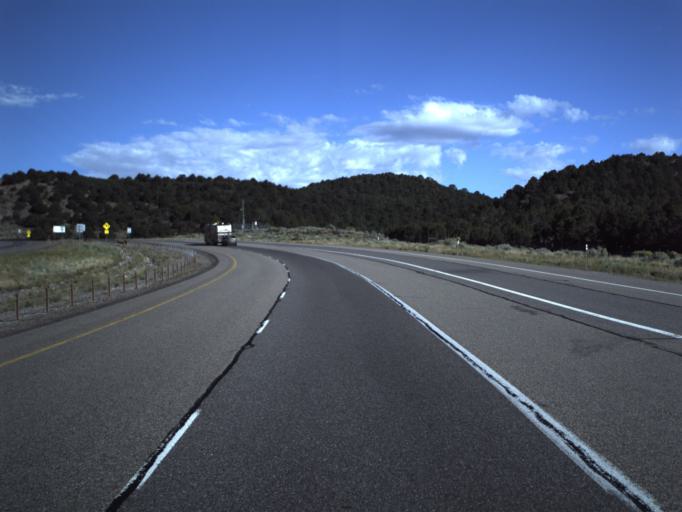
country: US
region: Utah
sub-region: Beaver County
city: Beaver
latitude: 38.5897
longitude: -112.4918
